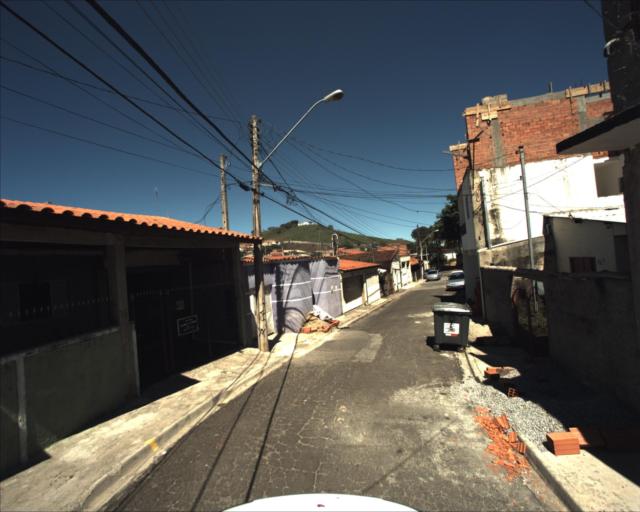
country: BR
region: Sao Paulo
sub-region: Votorantim
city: Votorantim
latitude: -23.5161
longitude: -47.4266
